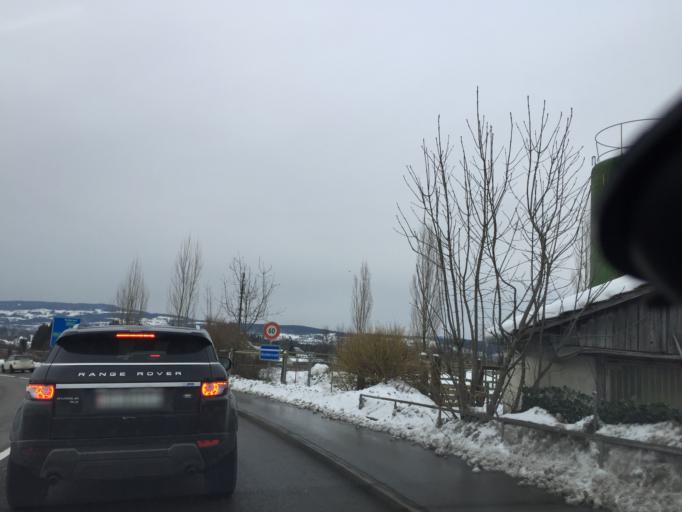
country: CH
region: Zurich
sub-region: Bezirk Horgen
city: Richterswil / Burghalde
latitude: 47.2000
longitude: 8.6878
